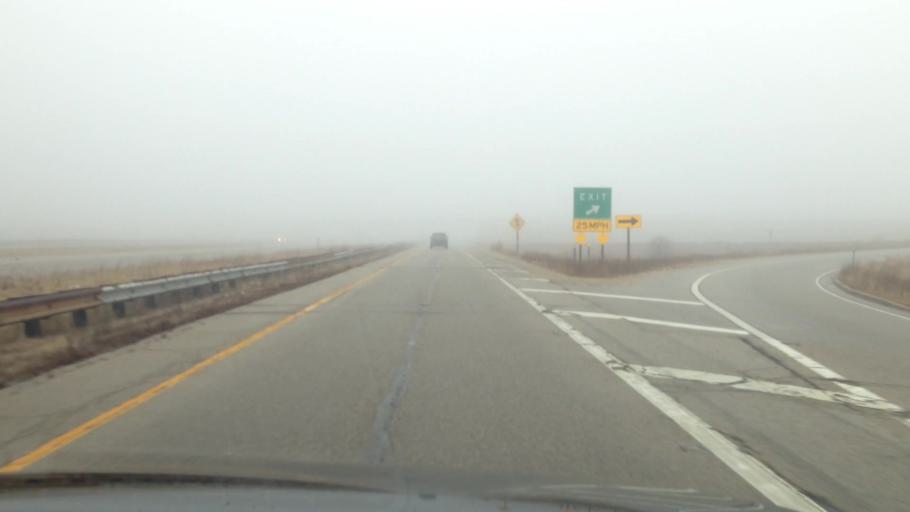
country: US
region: Wisconsin
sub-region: Walworth County
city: Elkhorn
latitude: 42.6671
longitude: -88.5162
